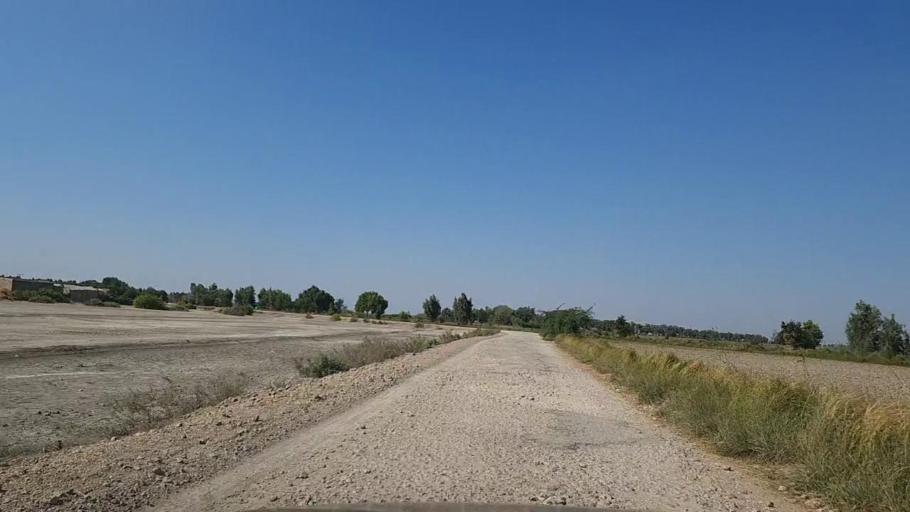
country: PK
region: Sindh
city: Mirpur Sakro
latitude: 24.6114
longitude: 67.7807
